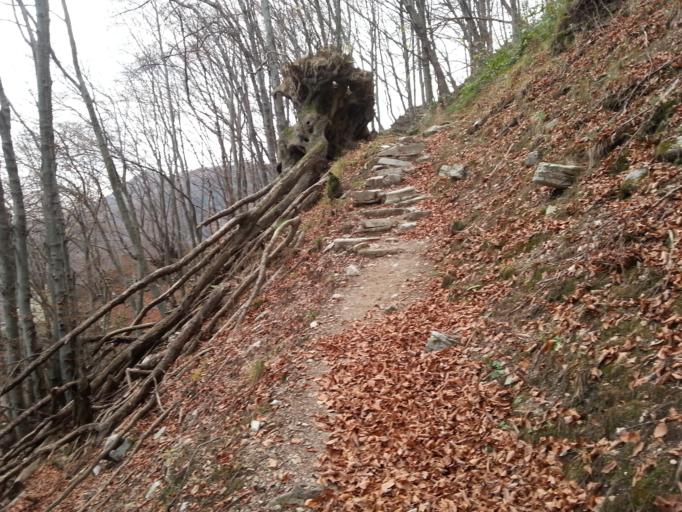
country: IT
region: Lombardy
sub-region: Provincia di Como
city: Casasco Intelvi
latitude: 45.9230
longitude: 9.0450
